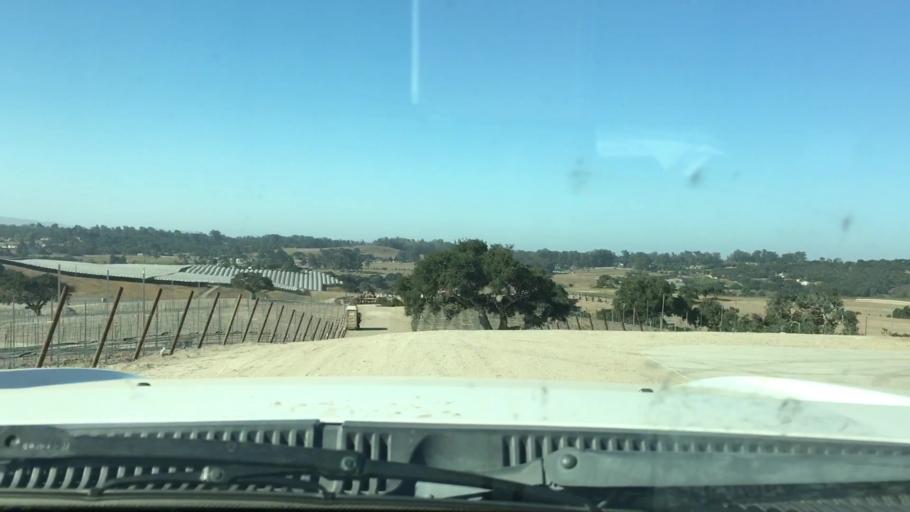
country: US
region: California
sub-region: San Luis Obispo County
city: Arroyo Grande
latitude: 35.1029
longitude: -120.5516
